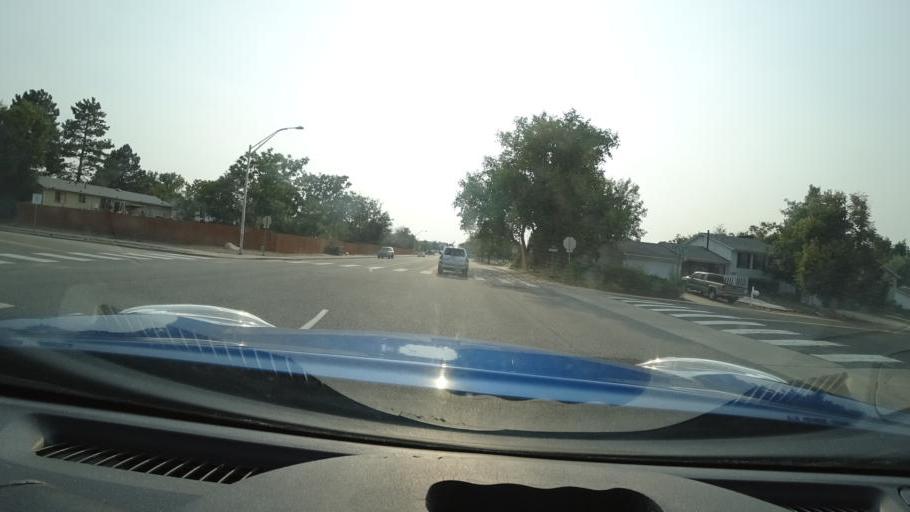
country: US
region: Colorado
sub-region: Adams County
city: Aurora
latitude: 39.6677
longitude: -104.8021
